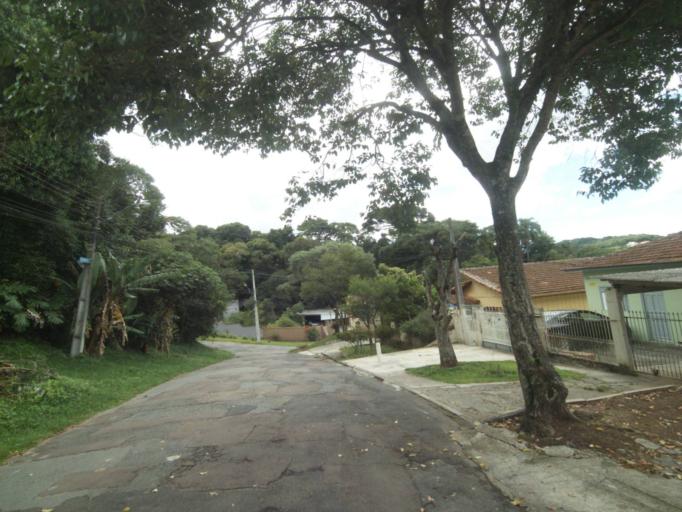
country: BR
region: Parana
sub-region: Curitiba
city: Curitiba
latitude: -25.4319
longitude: -49.3224
